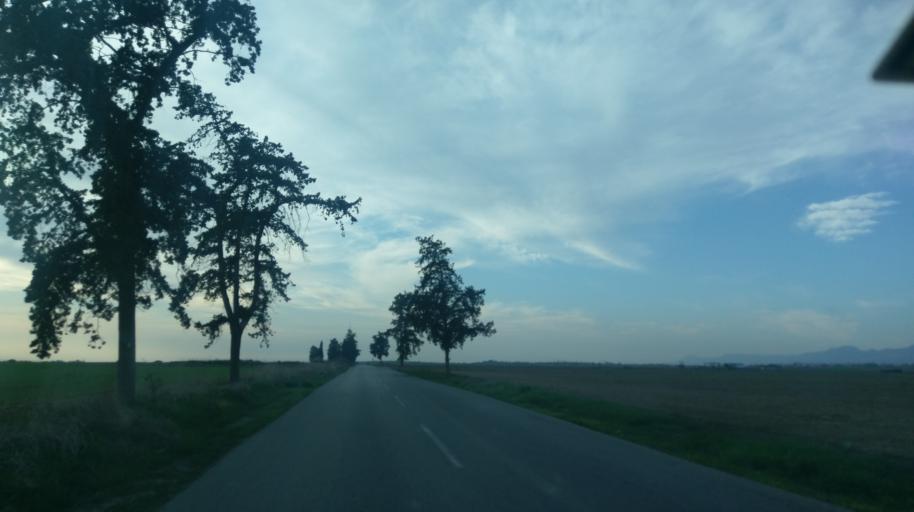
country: CY
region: Larnaka
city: Athienou
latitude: 35.1561
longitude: 33.5609
